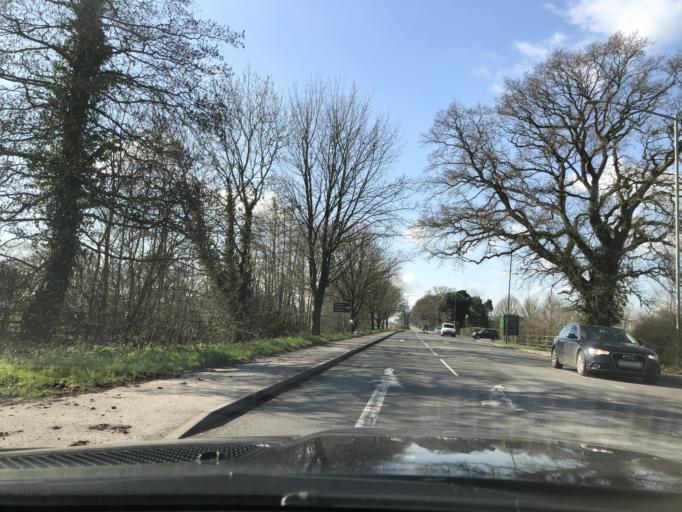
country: GB
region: England
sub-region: Warwickshire
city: Dunchurch
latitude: 52.3437
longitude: -1.3434
